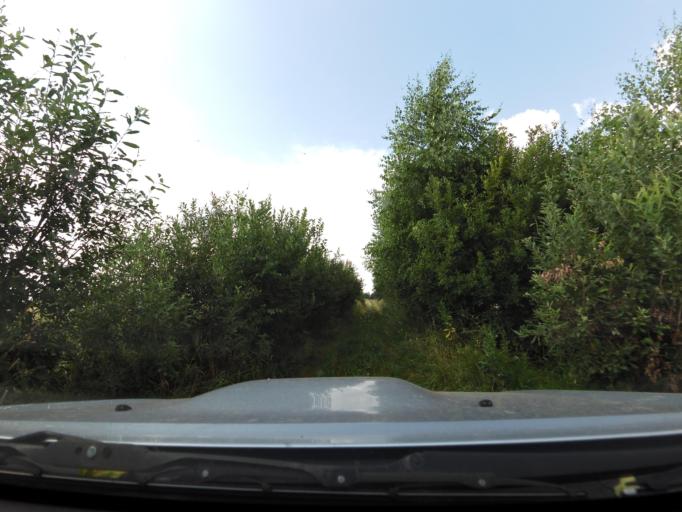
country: LT
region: Klaipedos apskritis
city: Silute
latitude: 55.4711
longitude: 21.4647
